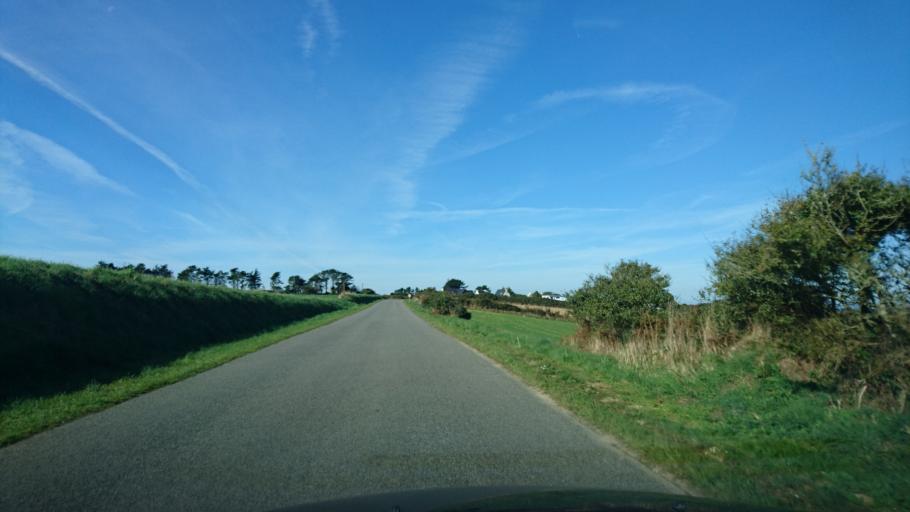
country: FR
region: Brittany
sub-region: Departement du Finistere
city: Lampaul-Plouarzel
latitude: 48.4306
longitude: -4.7641
